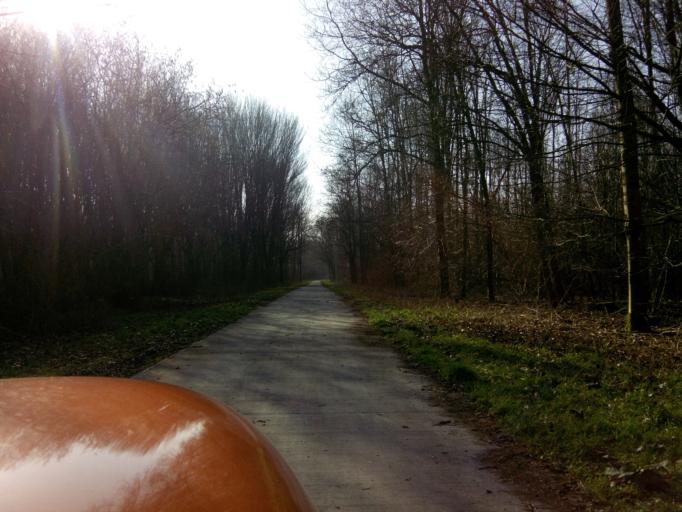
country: NL
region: Flevoland
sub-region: Gemeente Zeewolde
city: Zeewolde
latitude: 52.3326
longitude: 5.4959
